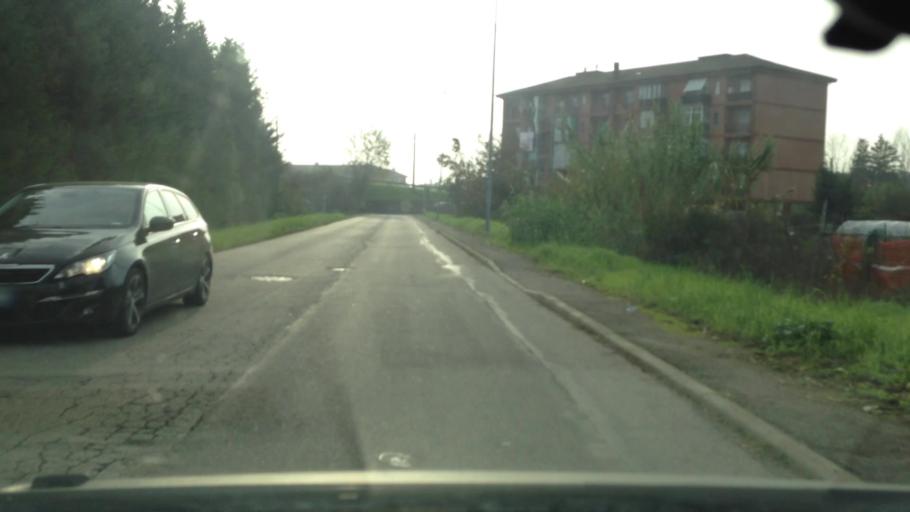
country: IT
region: Piedmont
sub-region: Provincia di Asti
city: Asti
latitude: 44.9011
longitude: 8.2306
